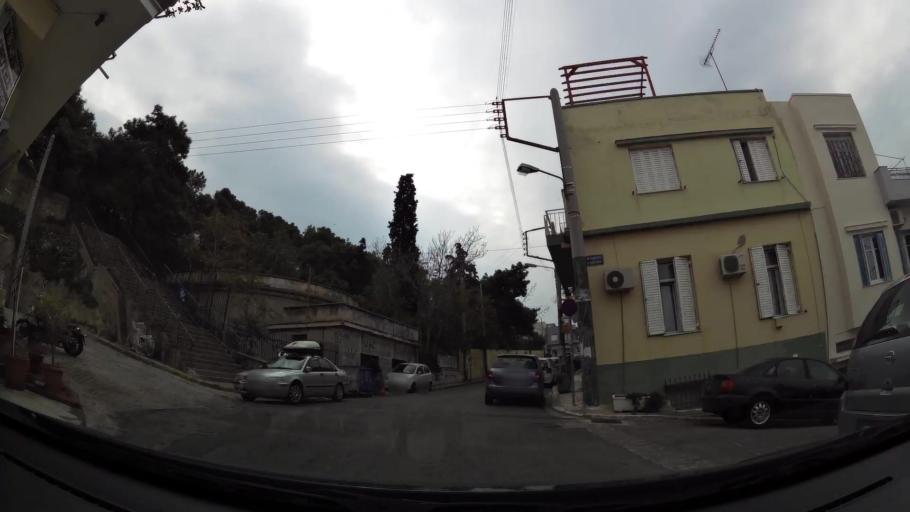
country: GR
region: Attica
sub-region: Nomos Attikis
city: Piraeus
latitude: 37.9412
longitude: 23.6550
